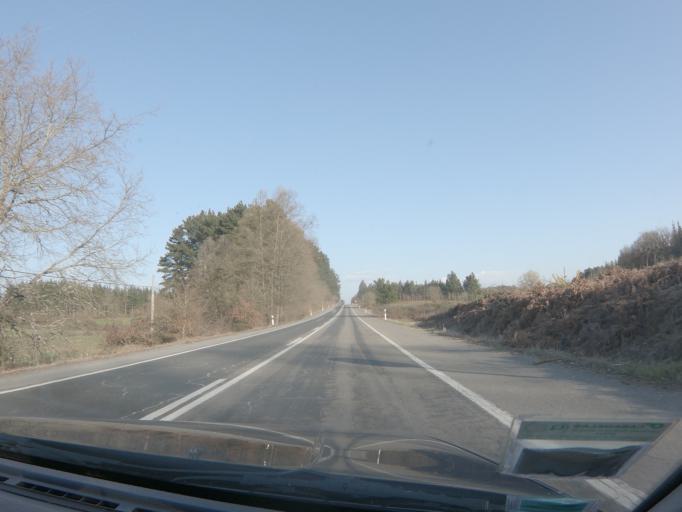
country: ES
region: Galicia
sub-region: Provincia de Lugo
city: Corgo
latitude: 42.9389
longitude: -7.4178
